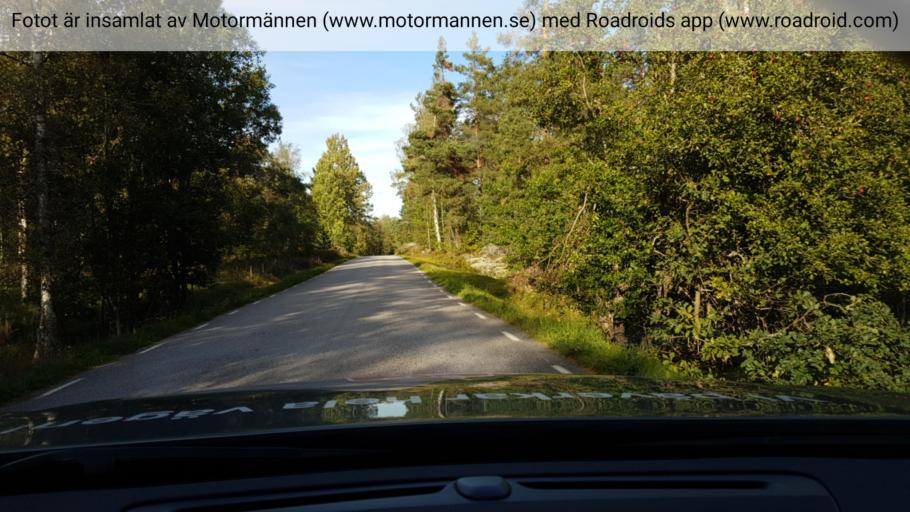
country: SE
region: OEstergoetland
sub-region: Valdemarsviks Kommun
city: Valdemarsvik
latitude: 58.0680
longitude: 16.6442
